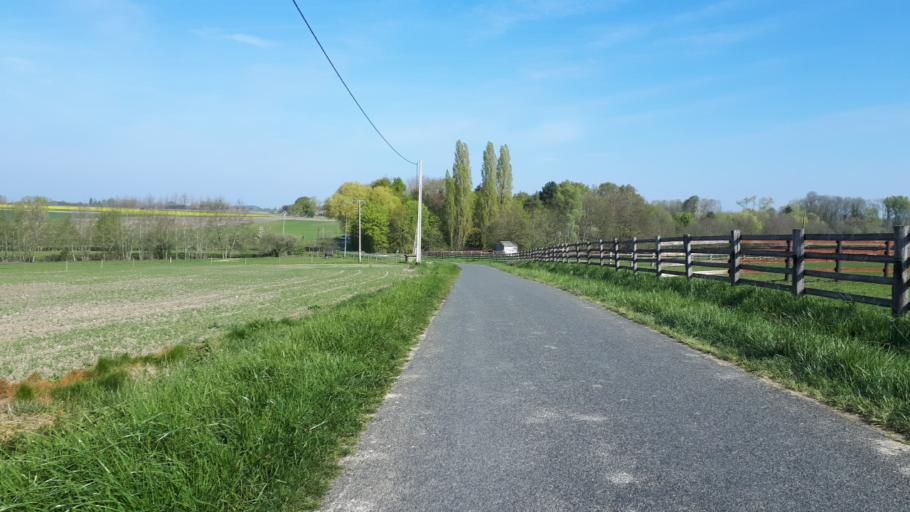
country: FR
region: Centre
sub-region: Departement du Loir-et-Cher
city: Contres
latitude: 47.3752
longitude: 1.3963
